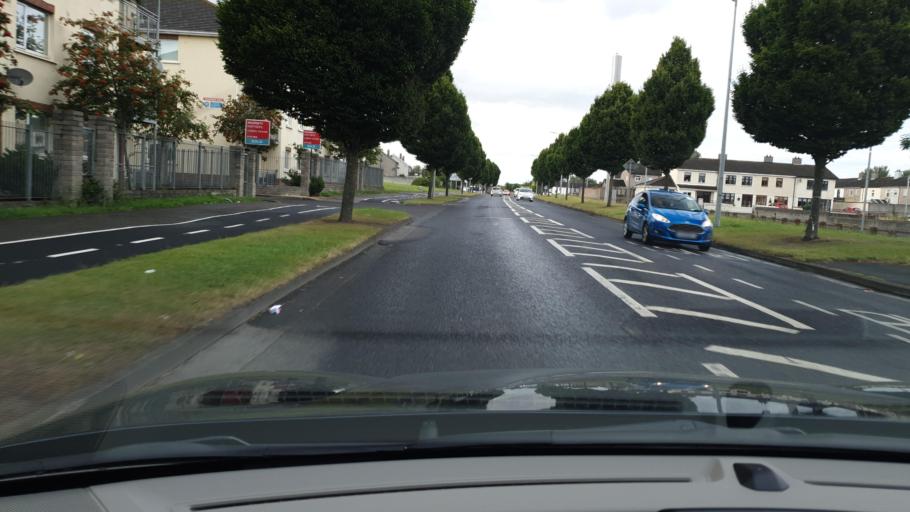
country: IE
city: Palmerstown
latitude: 53.3456
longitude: -6.3983
